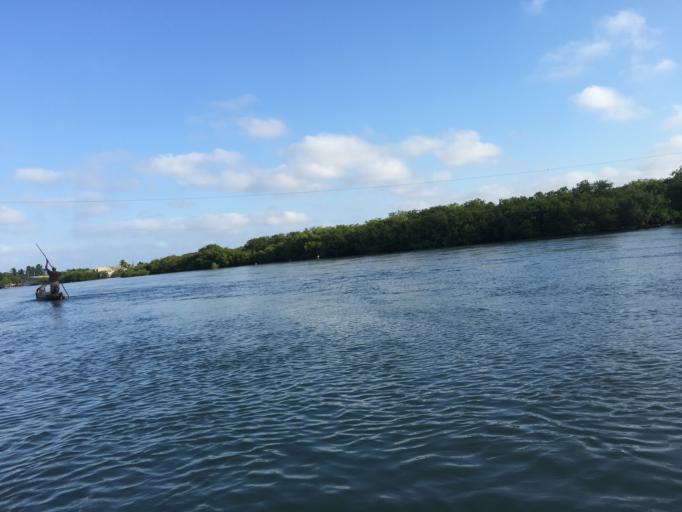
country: CO
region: Bolivar
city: Cartagena
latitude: 10.4860
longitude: -75.4889
